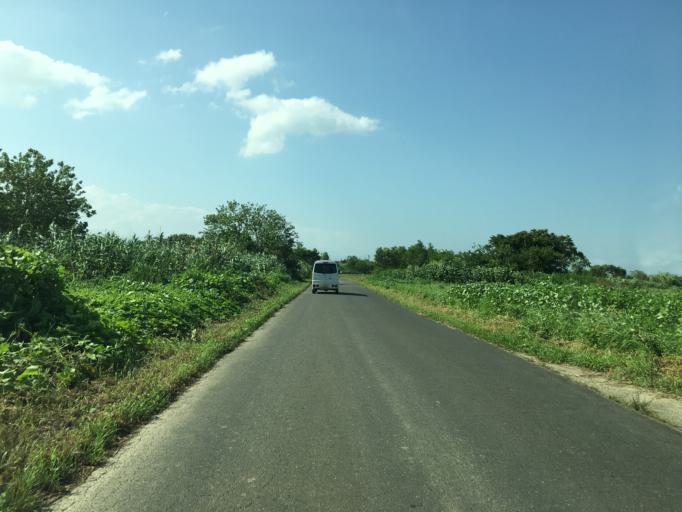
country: JP
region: Miyagi
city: Kakuda
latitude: 37.9635
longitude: 140.7891
